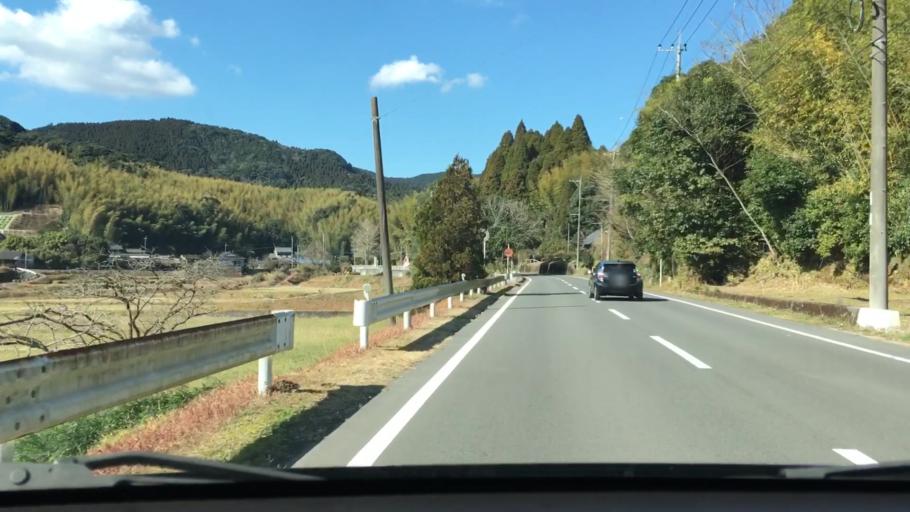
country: JP
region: Kagoshima
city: Ijuin
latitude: 31.7058
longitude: 130.4453
